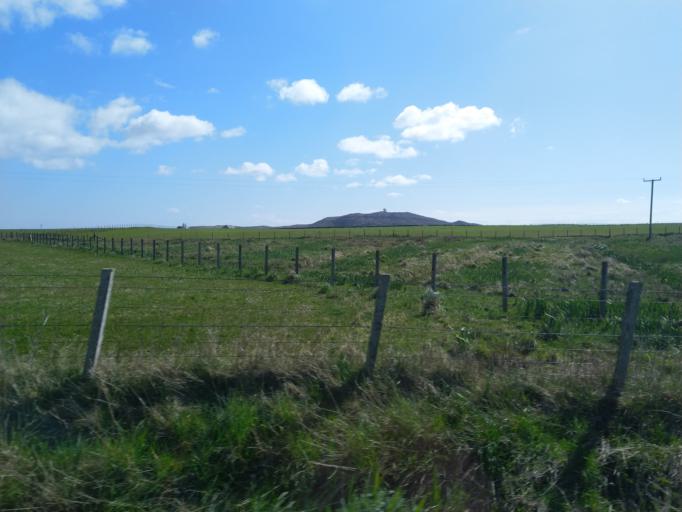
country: GB
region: Scotland
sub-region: Eilean Siar
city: Barra
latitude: 56.4836
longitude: -6.9120
